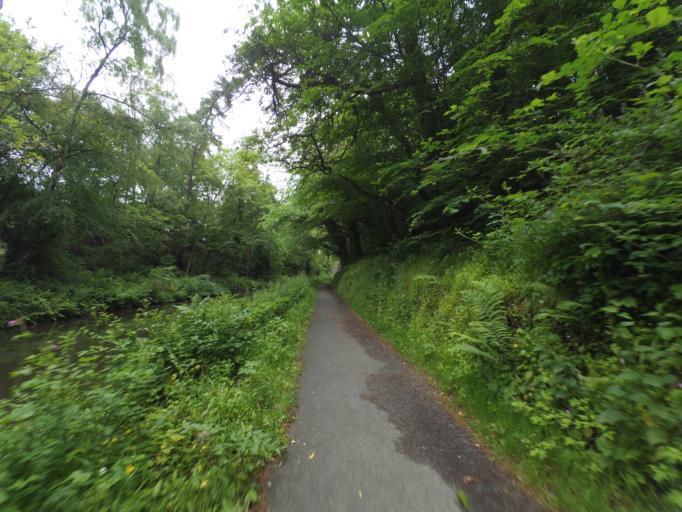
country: GB
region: Scotland
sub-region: Falkirk
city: Polmont
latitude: 55.9653
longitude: -3.6609
